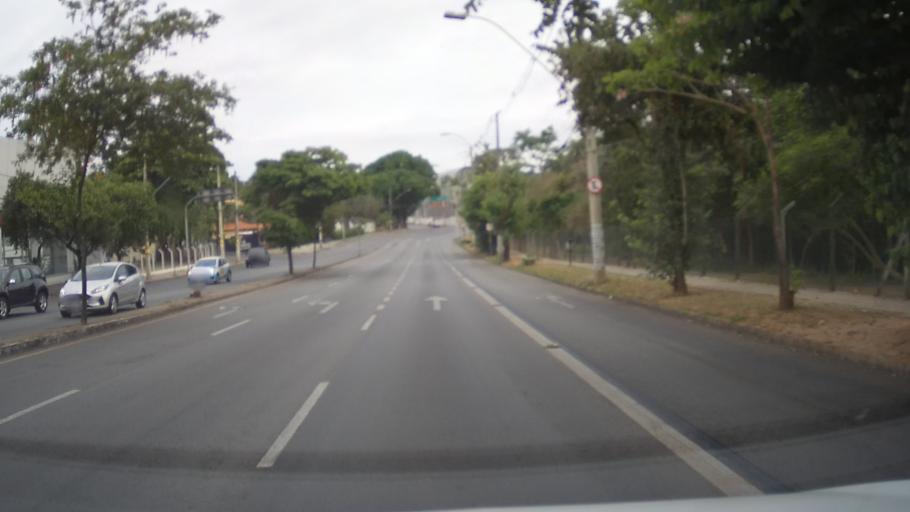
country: BR
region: Minas Gerais
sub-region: Belo Horizonte
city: Belo Horizonte
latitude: -19.8720
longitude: -43.9766
